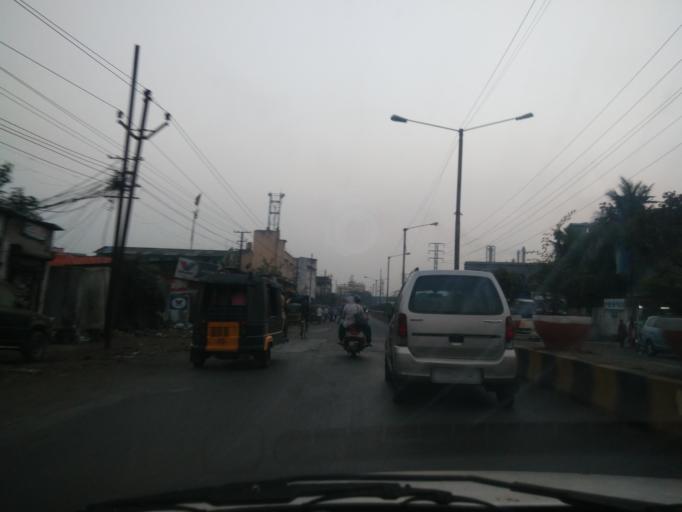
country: IN
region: Maharashtra
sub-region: Thane
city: Dombivli
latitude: 19.2143
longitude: 73.1161
